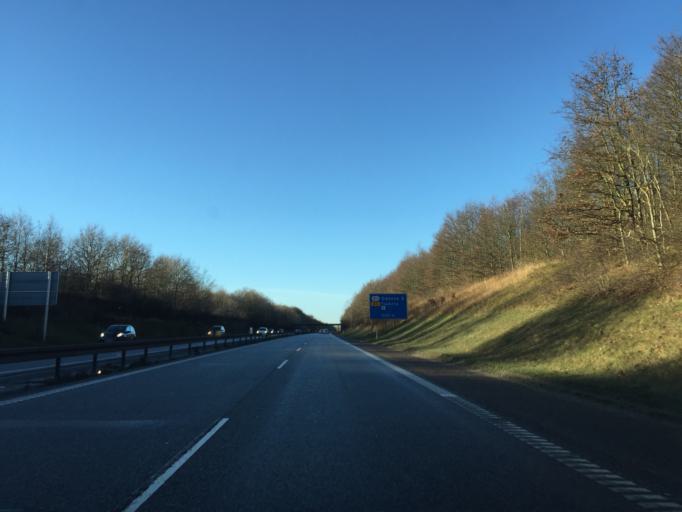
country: DK
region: South Denmark
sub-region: Odense Kommune
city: Hojby
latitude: 55.3518
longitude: 10.3958
